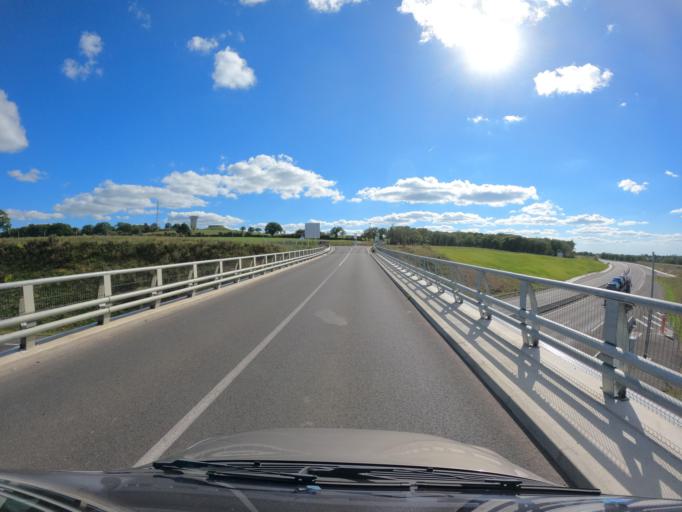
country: FR
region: Auvergne
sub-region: Departement de l'Allier
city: Buxieres-les-Mines
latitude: 46.3995
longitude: 3.0454
